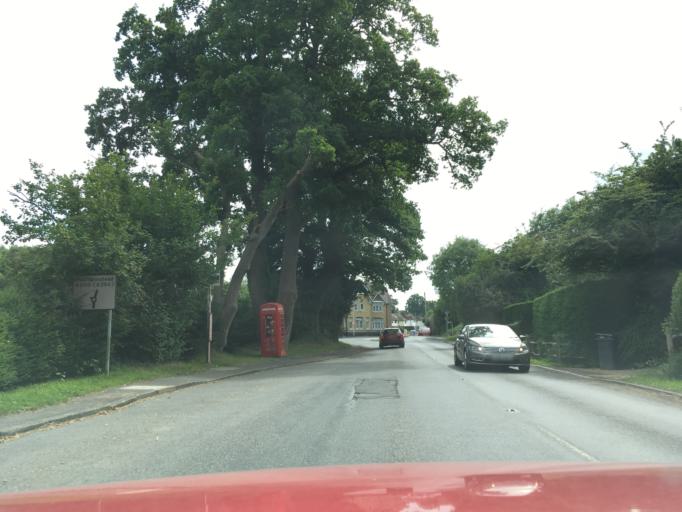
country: GB
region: England
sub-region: East Sussex
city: Crowborough
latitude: 51.1162
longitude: 0.1854
